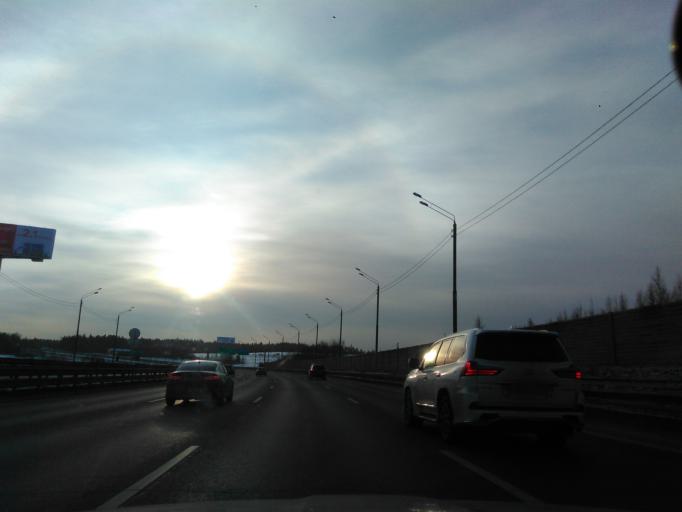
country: RU
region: Moskovskaya
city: Pavlovskaya Sloboda
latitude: 55.7876
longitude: 37.0606
